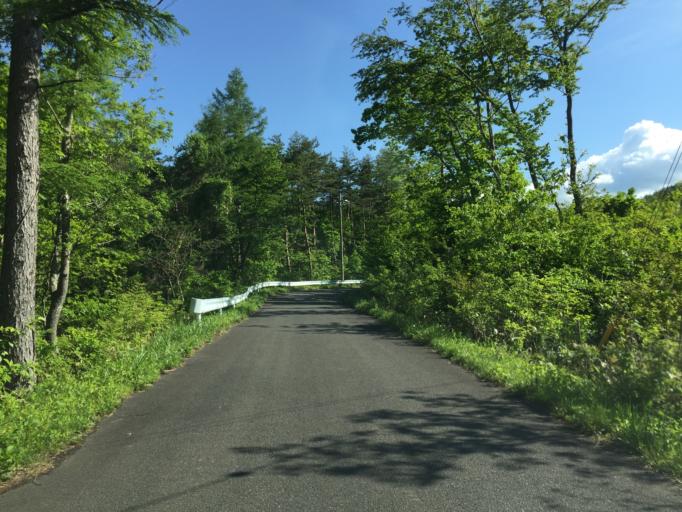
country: JP
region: Fukushima
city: Fukushima-shi
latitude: 37.7243
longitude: 140.3120
